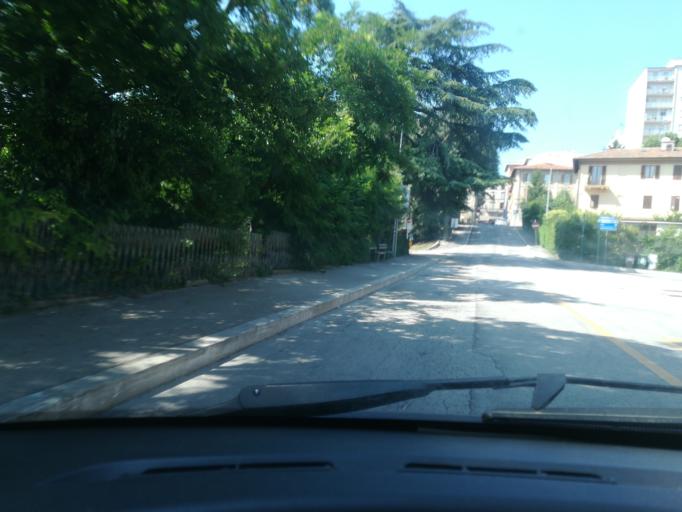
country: IT
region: The Marches
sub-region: Provincia di Macerata
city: Macerata
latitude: 43.2998
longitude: 13.4435
